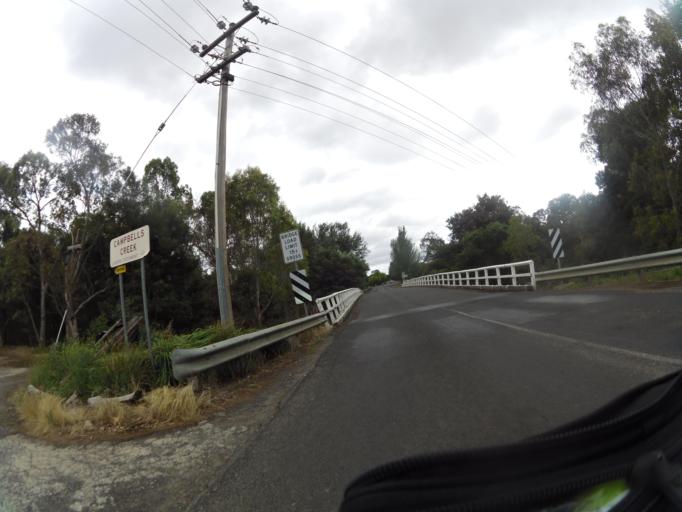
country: AU
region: Victoria
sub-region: Mount Alexander
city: Castlemaine
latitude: -37.0699
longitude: 144.2119
